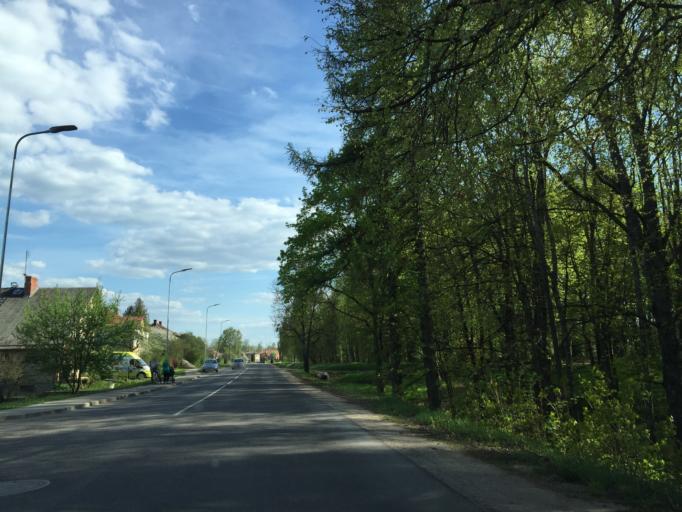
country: LV
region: Limbazu Rajons
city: Limbazi
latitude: 57.5061
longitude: 24.7145
